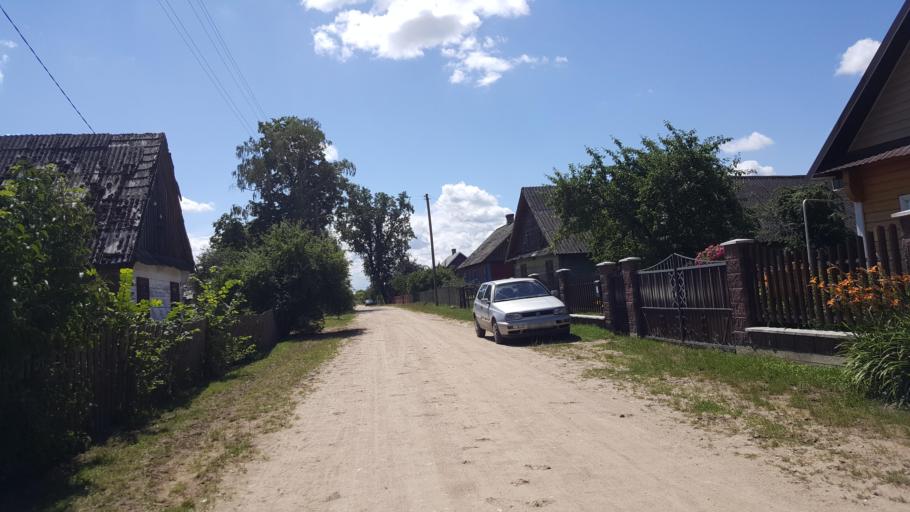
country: BY
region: Brest
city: Kamyanyets
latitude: 52.3282
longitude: 23.9132
